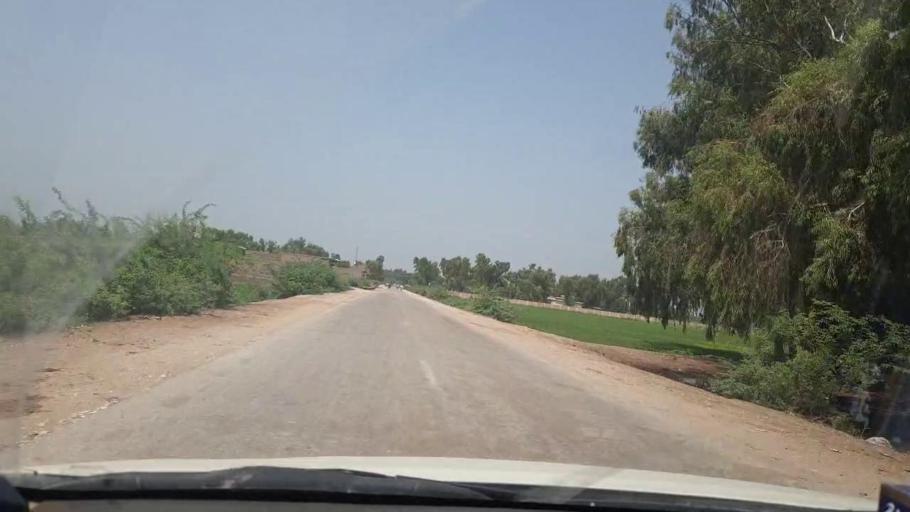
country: PK
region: Sindh
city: Shikarpur
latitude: 27.9543
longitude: 68.6622
